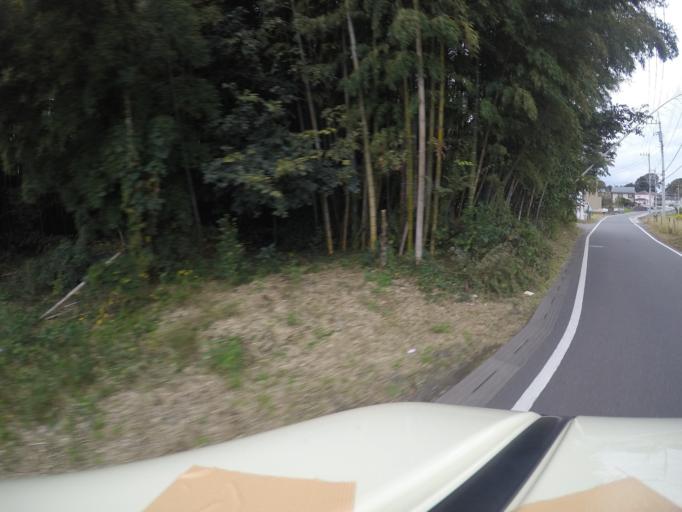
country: JP
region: Ibaraki
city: Naka
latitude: 36.0663
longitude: 140.1552
